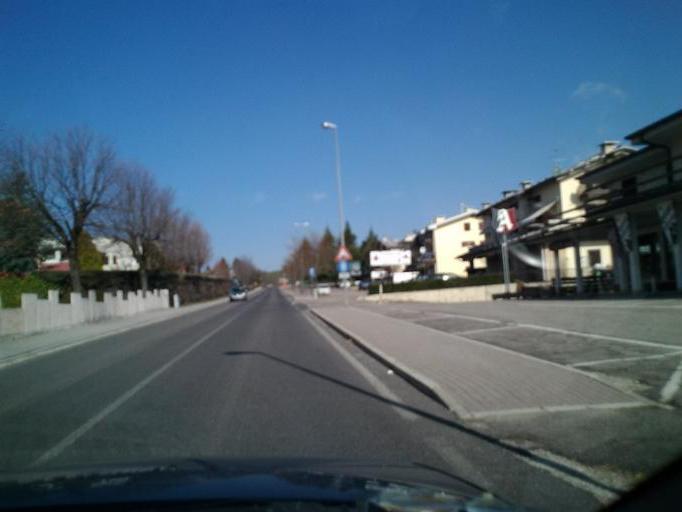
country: IT
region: Veneto
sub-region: Provincia di Verona
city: Cerro Veronese
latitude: 45.5800
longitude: 11.0422
